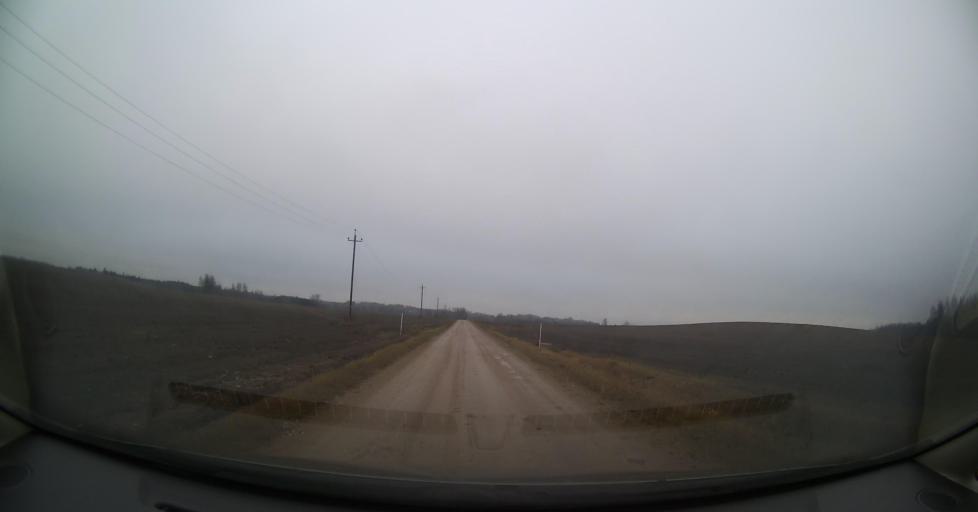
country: EE
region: Tartu
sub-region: Tartu linn
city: Tartu
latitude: 58.3895
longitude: 26.9993
